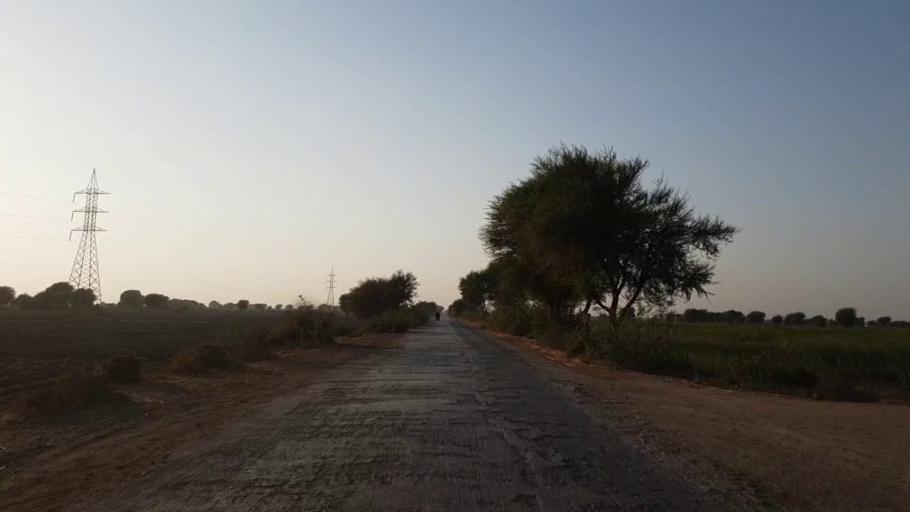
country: PK
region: Sindh
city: Chambar
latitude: 25.2166
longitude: 68.7596
